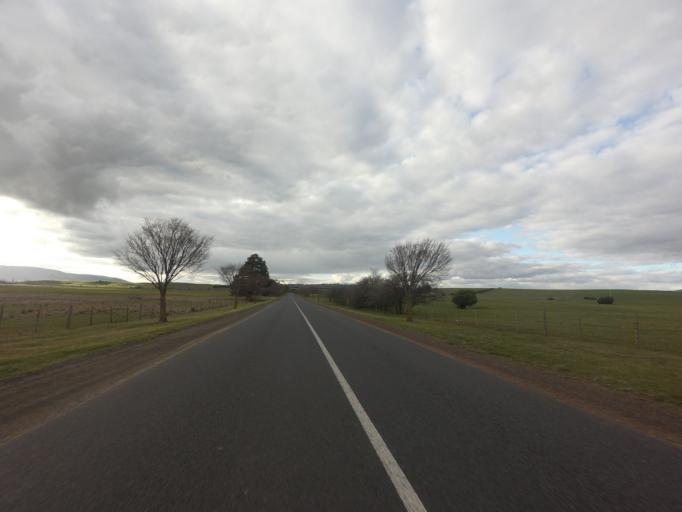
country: AU
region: Tasmania
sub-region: Northern Midlands
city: Evandale
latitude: -42.0241
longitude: 147.4931
